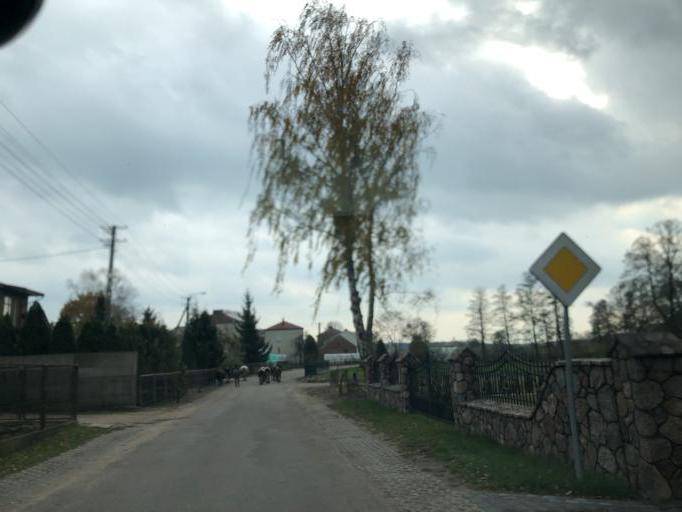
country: PL
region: Podlasie
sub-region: Lomza
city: Lomza
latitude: 53.1569
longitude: 22.0032
